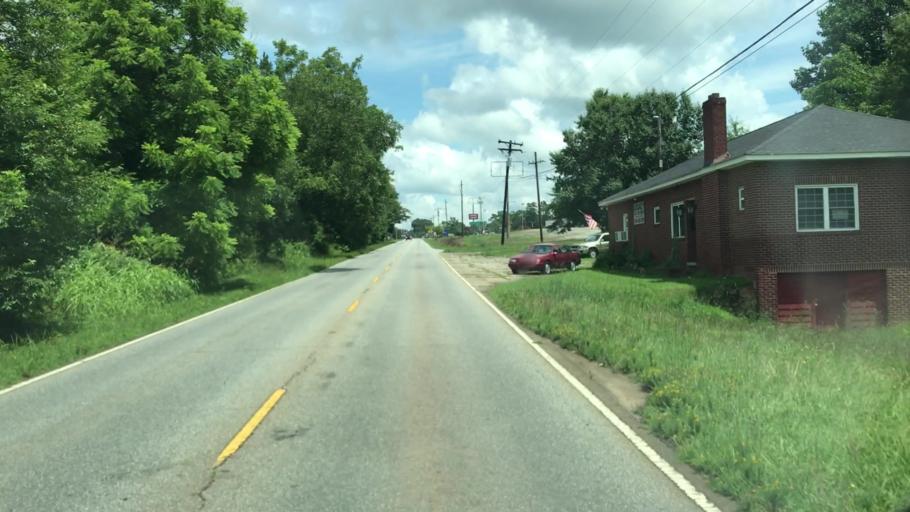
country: US
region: South Carolina
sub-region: Anderson County
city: Williamston
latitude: 34.6390
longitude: -82.4670
